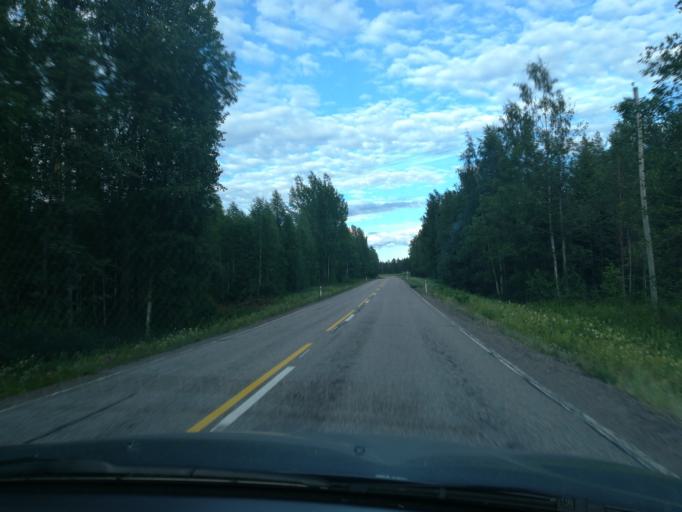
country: FI
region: Southern Savonia
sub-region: Mikkeli
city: Puumala
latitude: 61.5009
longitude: 27.8516
